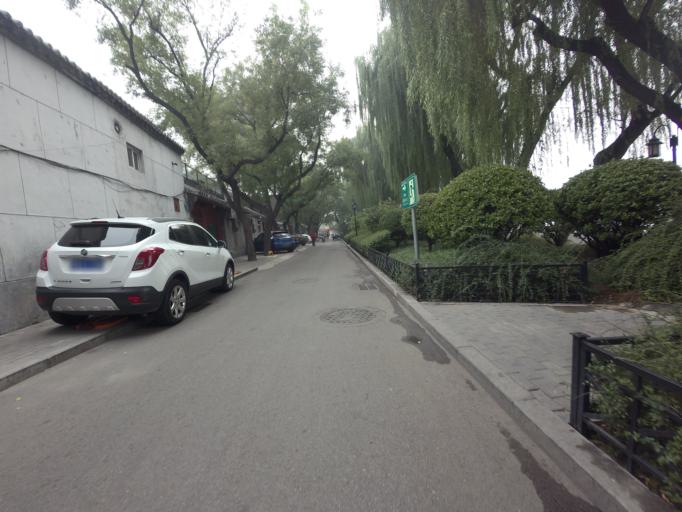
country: CN
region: Beijing
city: Jingshan
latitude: 39.9341
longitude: 116.3880
